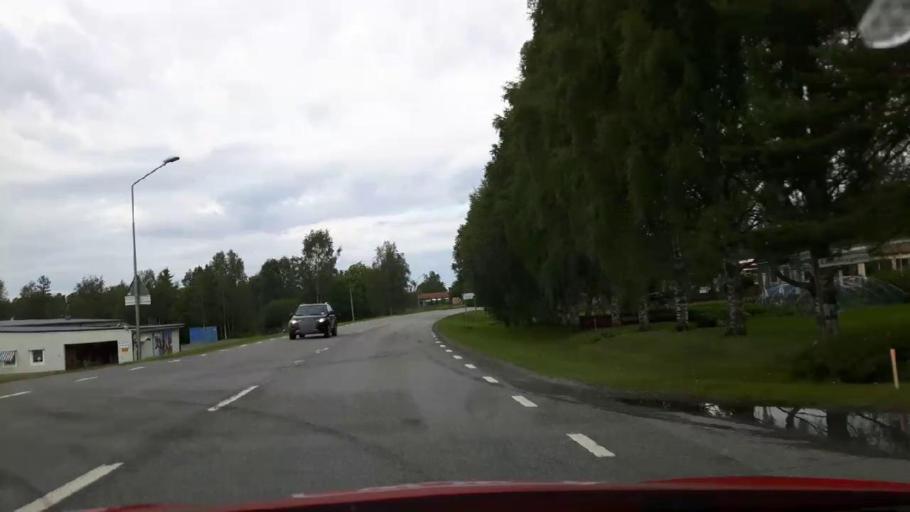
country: SE
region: Jaemtland
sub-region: Stroemsunds Kommun
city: Stroemsund
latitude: 63.5762
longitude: 15.3526
